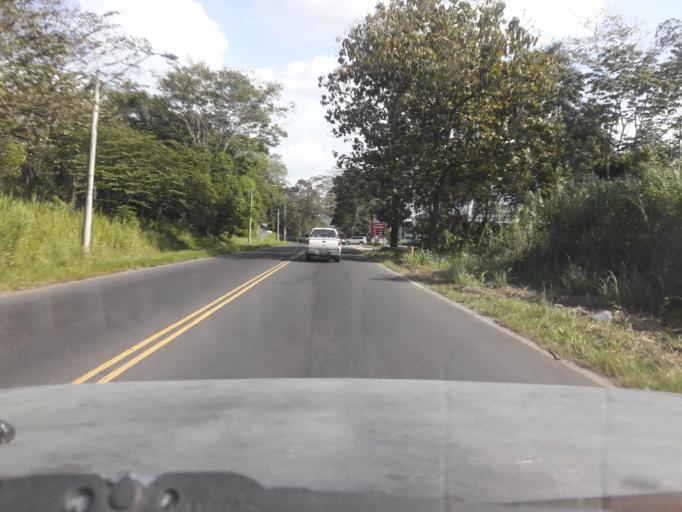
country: PA
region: Panama
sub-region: Distrito de Panama
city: Ancon
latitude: 8.9884
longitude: -79.5775
